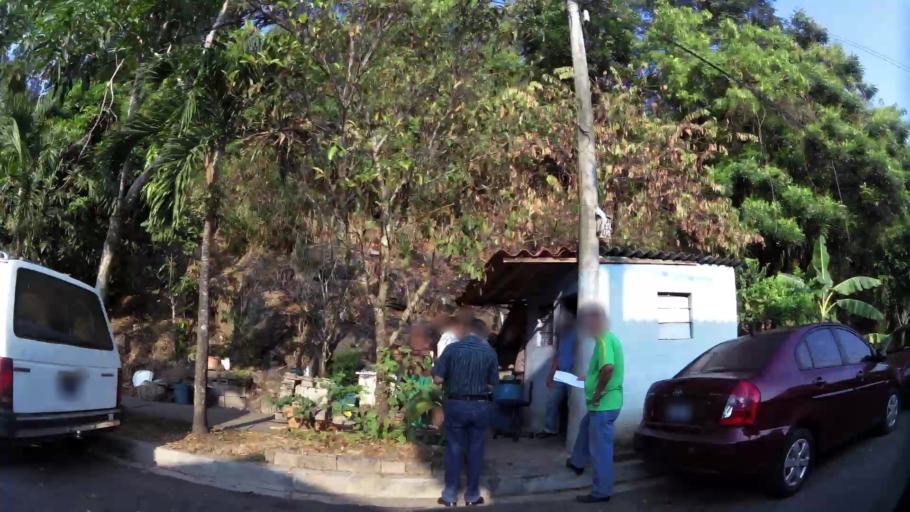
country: SV
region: San Salvador
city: San Salvador
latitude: 13.6820
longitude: -89.2027
